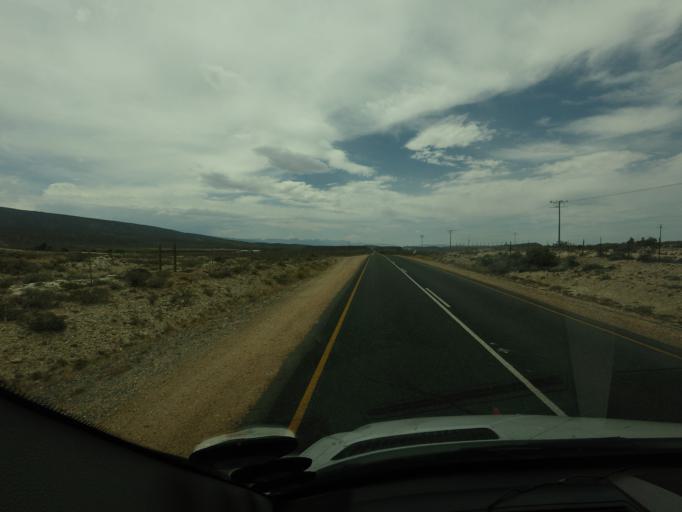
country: ZA
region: Western Cape
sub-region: Overberg District Municipality
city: Swellendam
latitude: -33.8438
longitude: 20.8646
